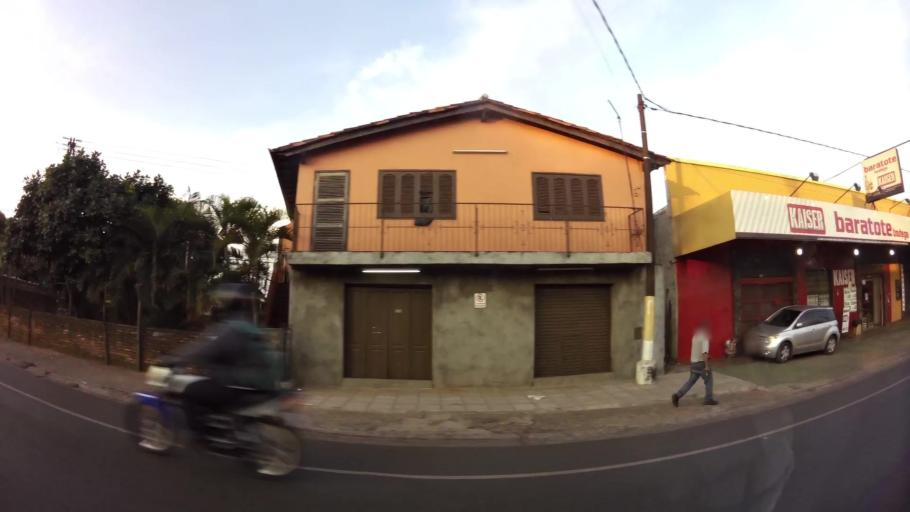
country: PY
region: Central
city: San Lorenzo
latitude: -25.3476
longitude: -57.4971
